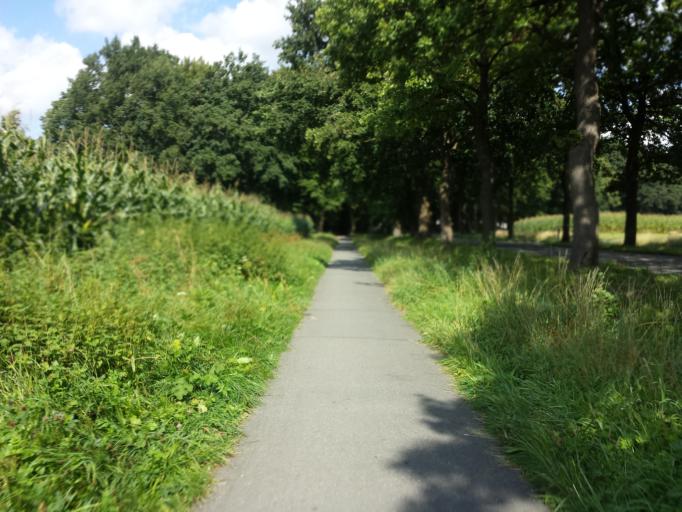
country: DE
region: North Rhine-Westphalia
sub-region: Regierungsbezirk Detmold
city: Guetersloh
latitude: 51.8948
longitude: 8.3957
